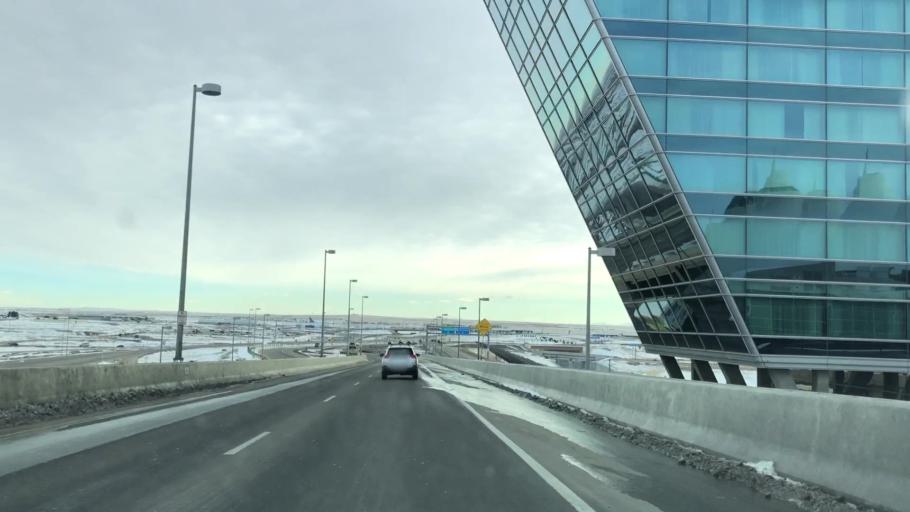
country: US
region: Colorado
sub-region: Weld County
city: Lochbuie
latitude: 39.8479
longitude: -104.6728
